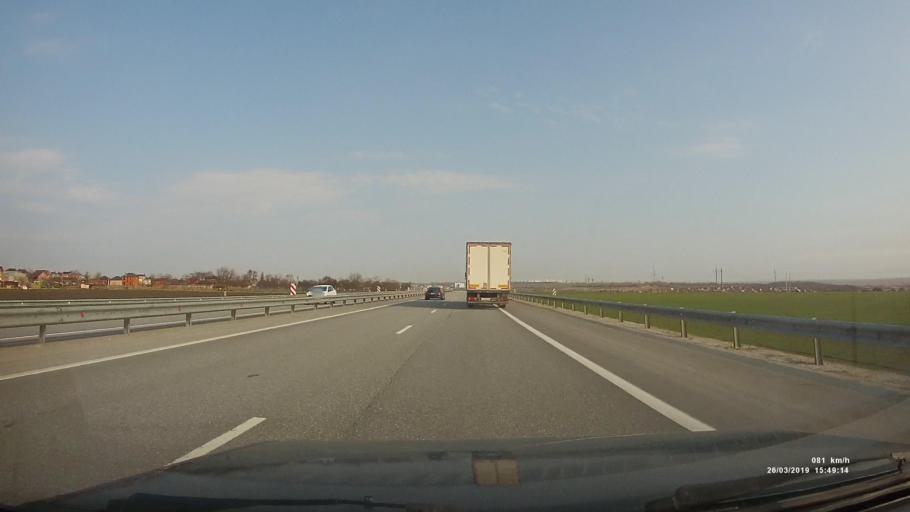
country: RU
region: Rostov
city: Chaltyr
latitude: 47.2768
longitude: 39.4658
